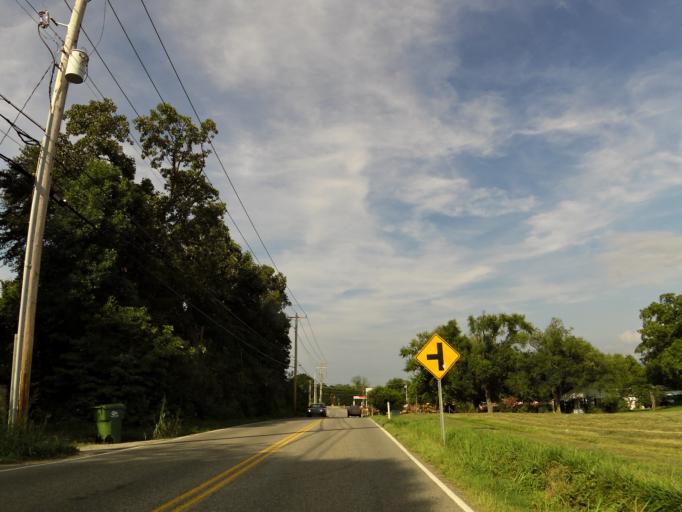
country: US
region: Tennessee
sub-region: Blount County
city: Eagleton Village
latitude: 35.7687
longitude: -83.9196
